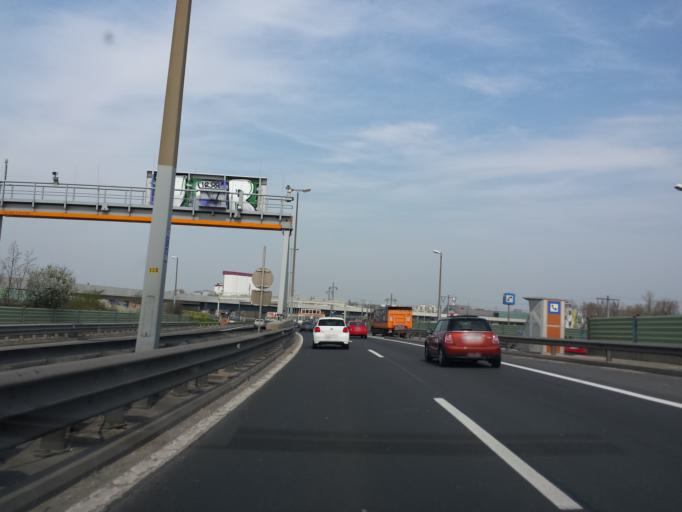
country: AT
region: Vienna
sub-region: Wien Stadt
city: Vienna
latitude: 48.2154
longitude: 16.4472
